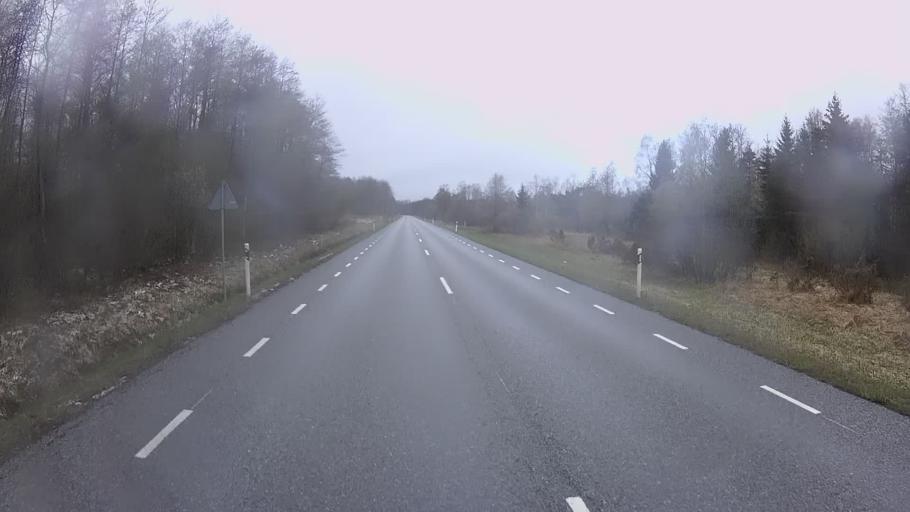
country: EE
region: Hiiumaa
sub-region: Kaerdla linn
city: Kardla
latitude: 59.0024
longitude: 22.5815
